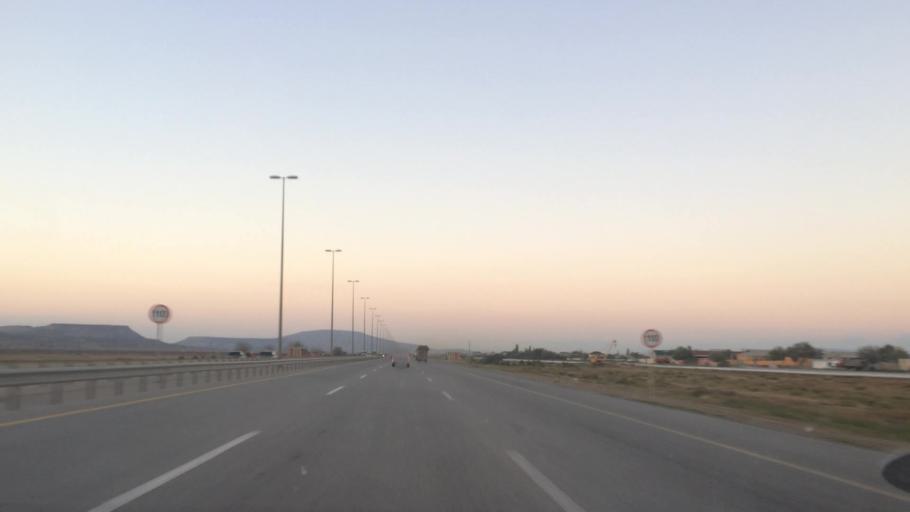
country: AZ
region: Baki
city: Qobustan
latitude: 40.0142
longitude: 49.4266
